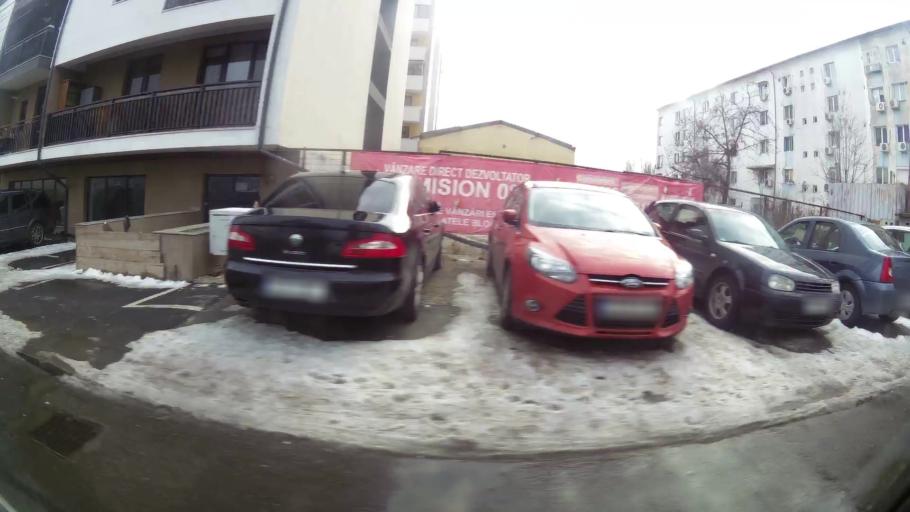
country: RO
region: Ilfov
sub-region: Comuna Popesti-Leordeni
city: Popesti-Leordeni
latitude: 44.4069
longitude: 26.1794
